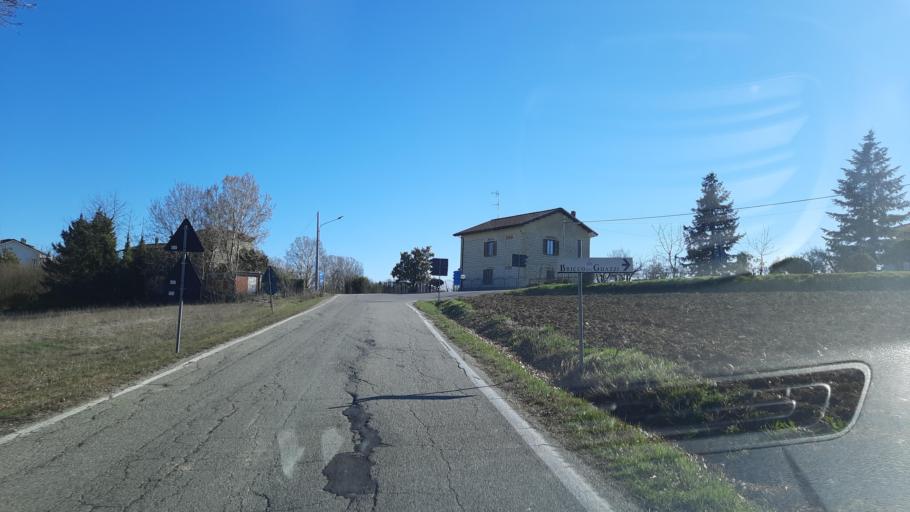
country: IT
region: Piedmont
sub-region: Provincia di Alessandria
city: Frassinello Monferrato
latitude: 45.0391
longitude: 8.3803
